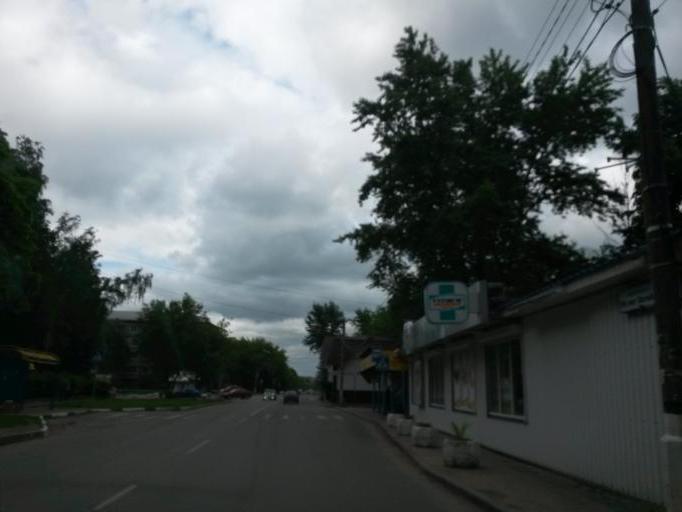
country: RU
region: Moskovskaya
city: Klimovsk
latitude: 55.3692
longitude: 37.5378
